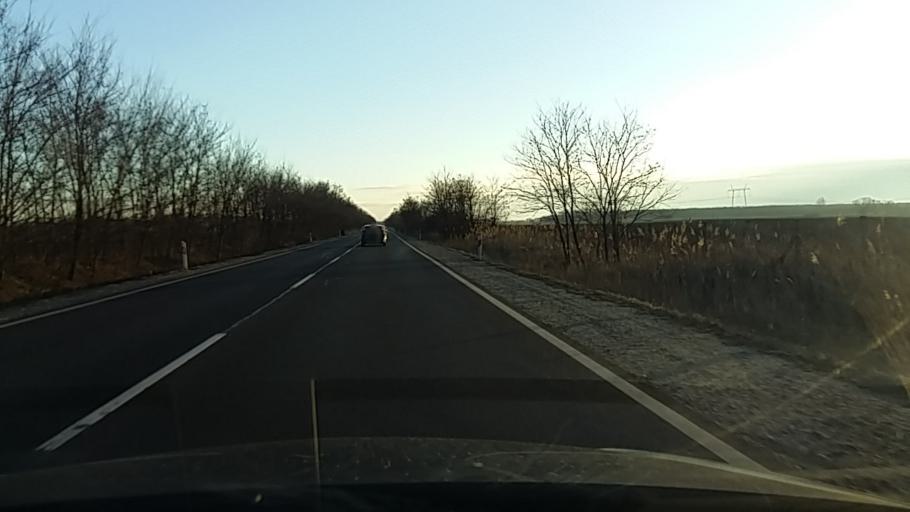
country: HU
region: Hajdu-Bihar
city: Teglas
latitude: 47.7515
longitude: 21.6772
